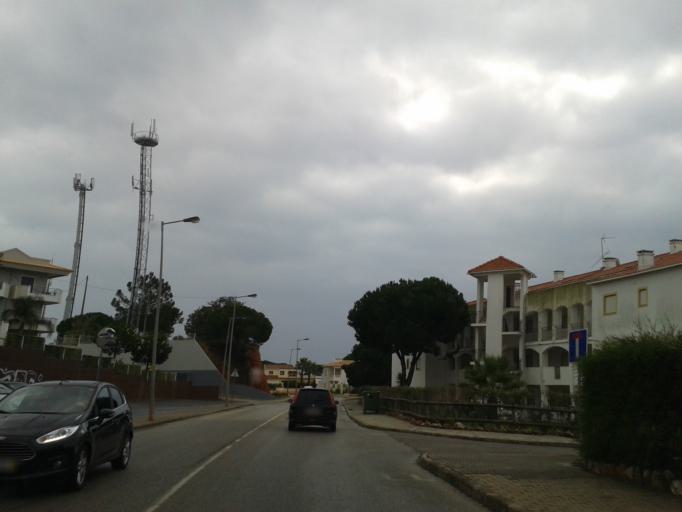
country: PT
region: Faro
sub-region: Loule
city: Boliqueime
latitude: 37.1003
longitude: -8.1843
